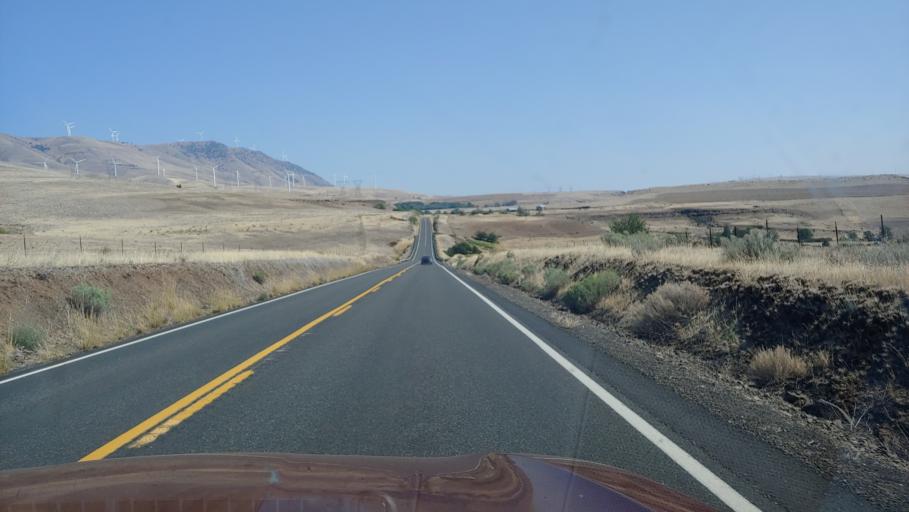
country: US
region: Washington
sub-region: Klickitat County
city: Goldendale
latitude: 45.6990
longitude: -120.8090
